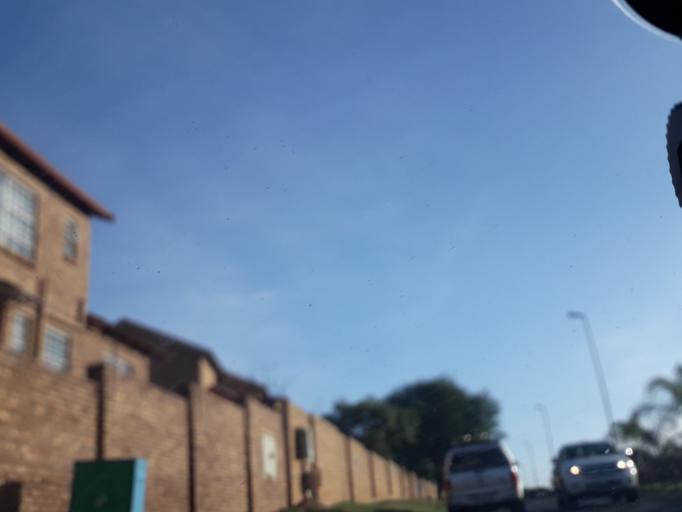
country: ZA
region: Gauteng
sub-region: City of Johannesburg Metropolitan Municipality
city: Roodepoort
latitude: -26.1058
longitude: 27.8944
